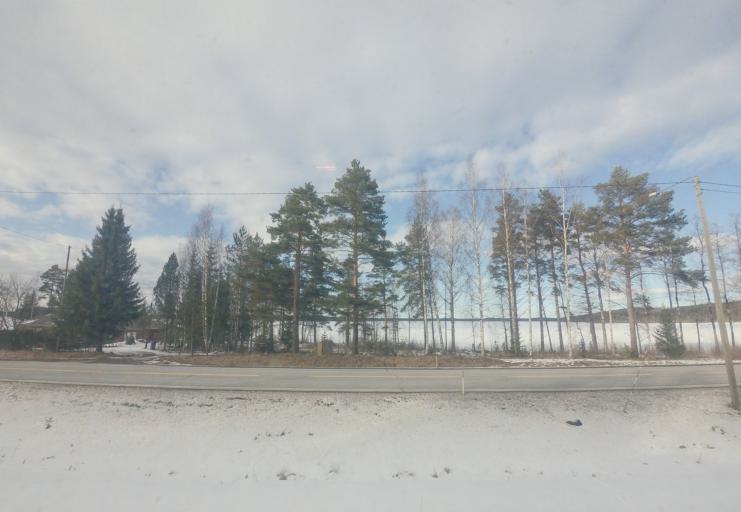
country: FI
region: Southern Savonia
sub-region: Savonlinna
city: Kerimaeki
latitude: 61.8057
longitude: 29.2842
